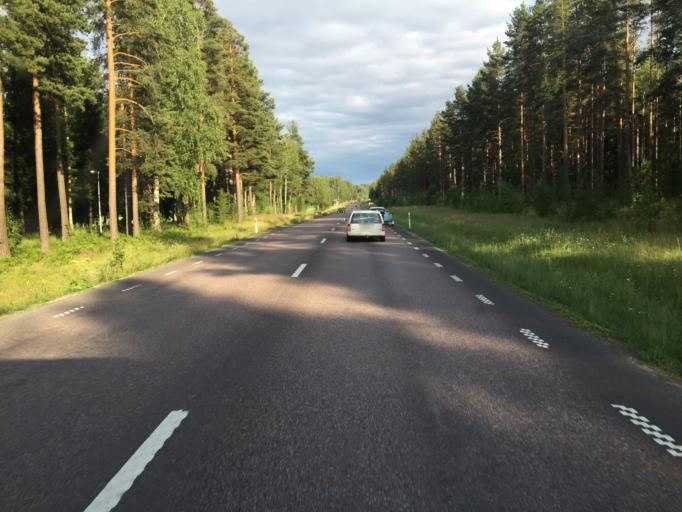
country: SE
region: Dalarna
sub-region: Borlange Kommun
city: Borlaenge
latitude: 60.5225
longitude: 15.3587
